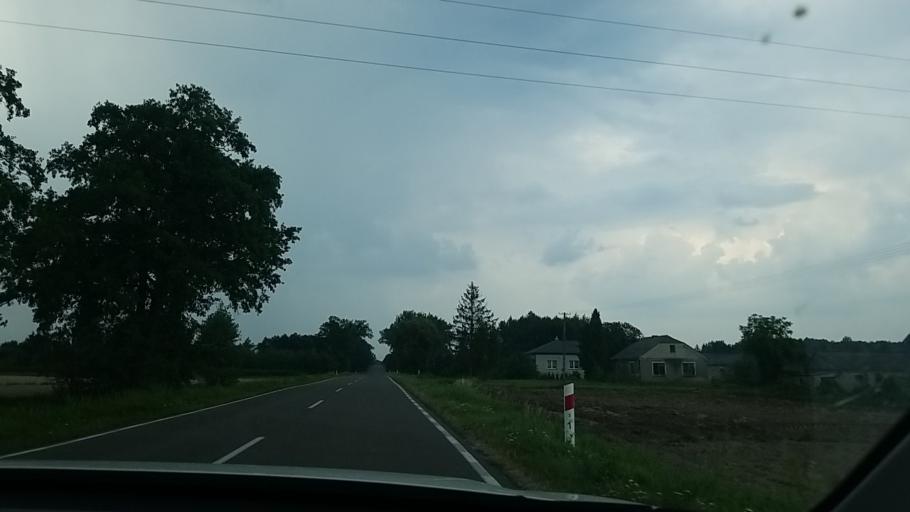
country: PL
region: Lublin Voivodeship
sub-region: Powiat leczynski
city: Cycow
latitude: 51.2627
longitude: 23.0942
